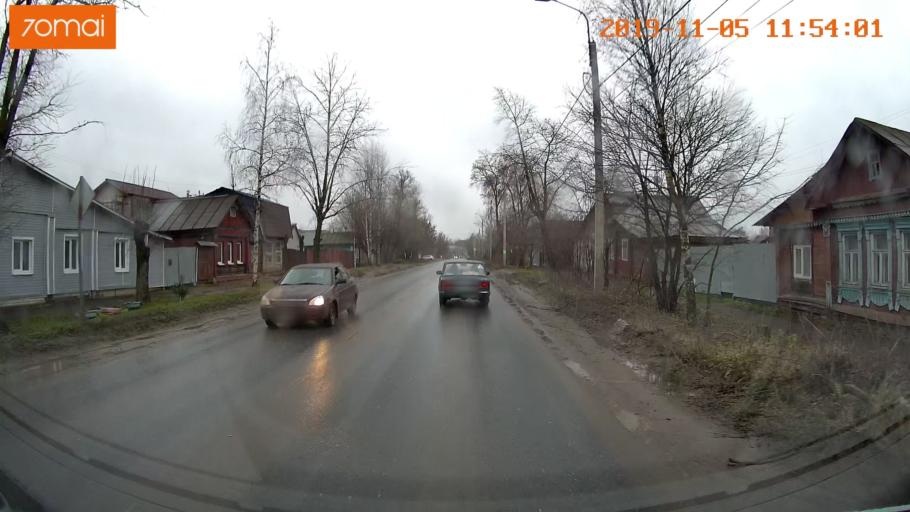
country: RU
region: Ivanovo
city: Bogorodskoye
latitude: 56.9934
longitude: 41.0308
